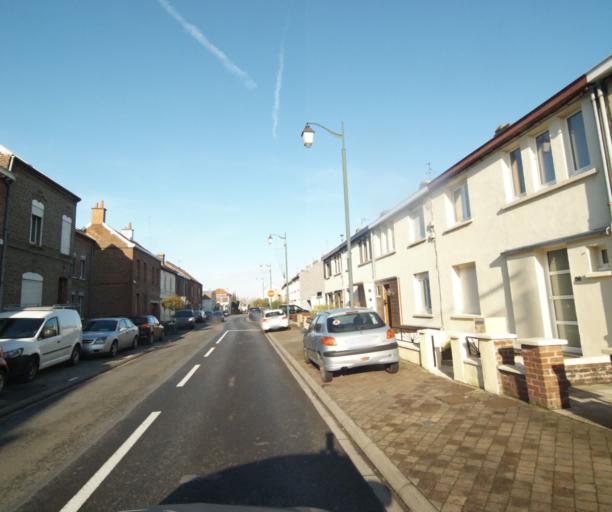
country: FR
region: Nord-Pas-de-Calais
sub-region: Departement du Nord
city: Aulnoy-lez-Valenciennes
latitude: 50.3355
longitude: 3.5276
